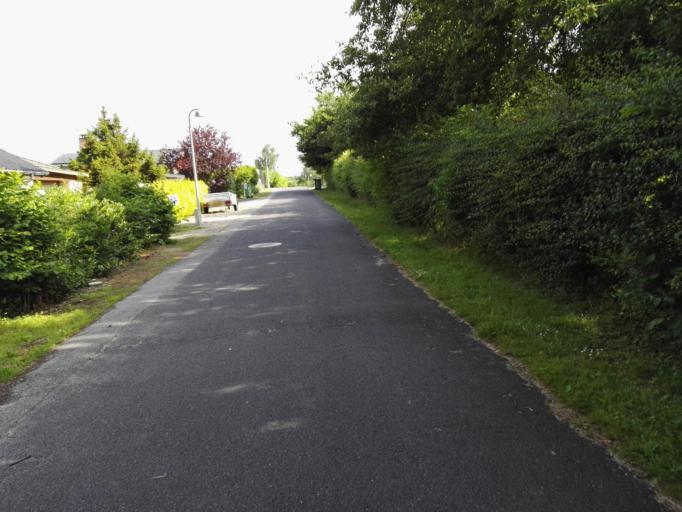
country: DK
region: Zealand
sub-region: Roskilde Kommune
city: Jyllinge
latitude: 55.7675
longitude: 12.1052
